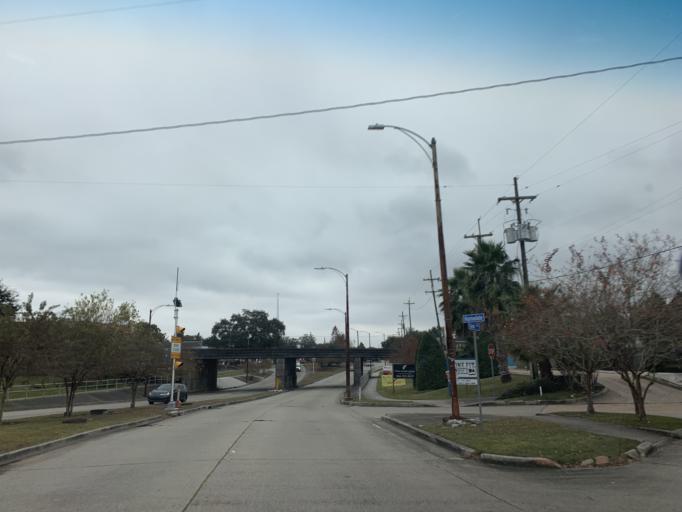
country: US
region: Louisiana
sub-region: Jefferson Parish
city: Metairie
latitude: 29.9921
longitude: -90.1097
